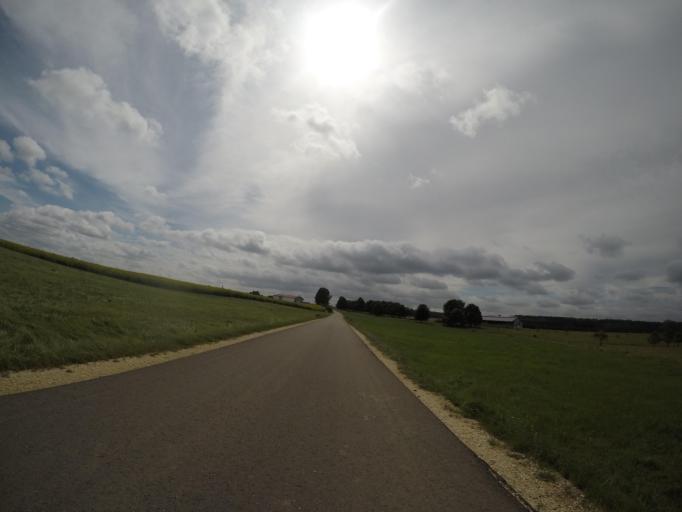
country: DE
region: Baden-Wuerttemberg
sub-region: Tuebingen Region
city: Schelklingen
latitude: 48.4251
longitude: 9.7280
